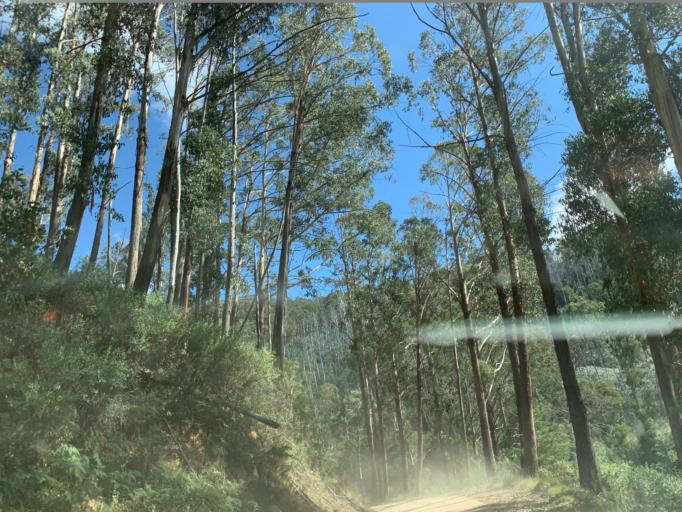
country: AU
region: Victoria
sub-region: Mansfield
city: Mansfield
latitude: -37.1007
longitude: 146.4831
